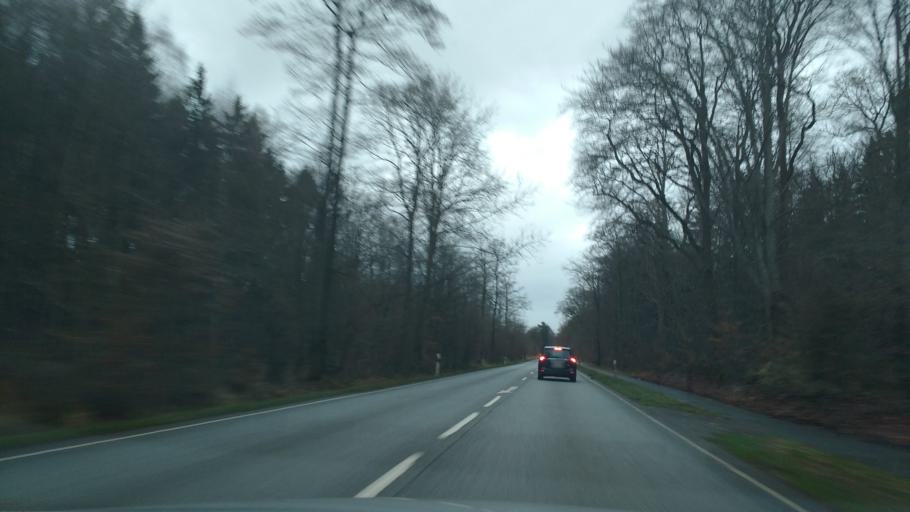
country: DE
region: Schleswig-Holstein
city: Oelixdorf
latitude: 53.9468
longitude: 9.5461
